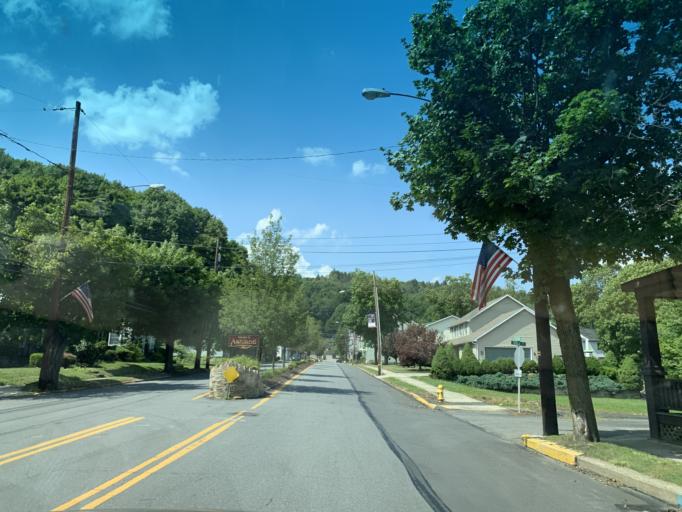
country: US
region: Pennsylvania
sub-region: Schuylkill County
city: Ashland
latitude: 40.7809
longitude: -76.3364
